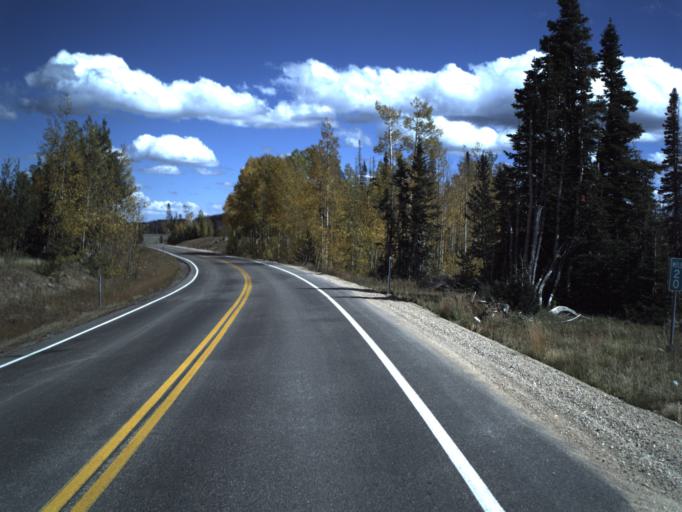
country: US
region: Utah
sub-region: Iron County
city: Parowan
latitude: 37.5702
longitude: -112.8050
